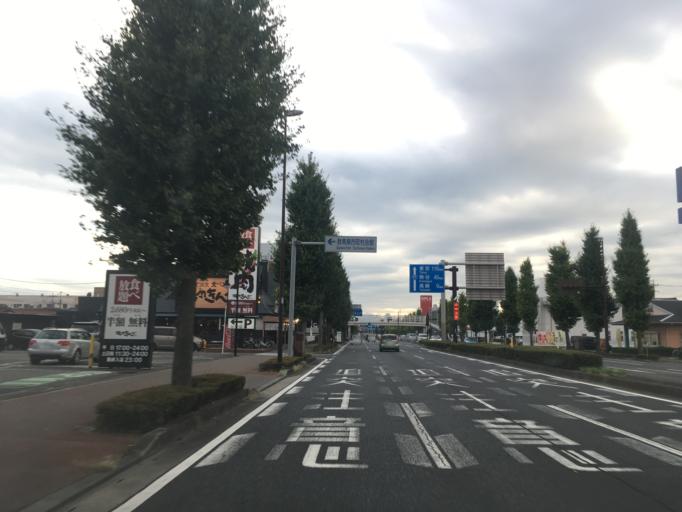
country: JP
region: Gunma
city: Maebashi-shi
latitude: 36.3844
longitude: 139.0443
